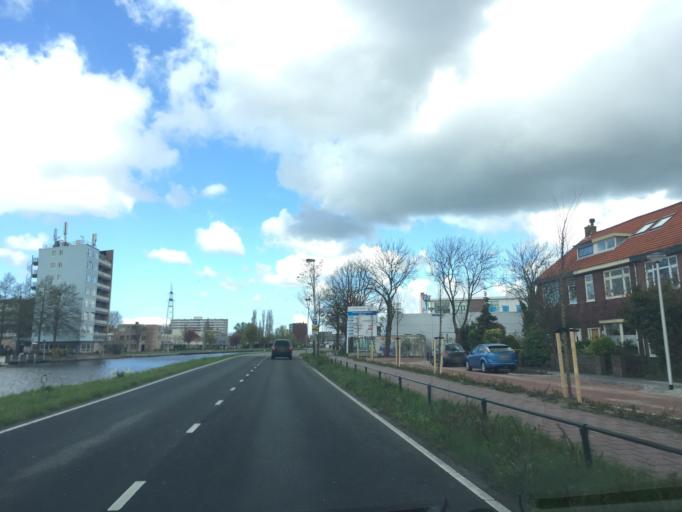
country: NL
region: South Holland
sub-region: Gemeente Leiderdorp
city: Leiderdorp
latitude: 52.1628
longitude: 4.5153
